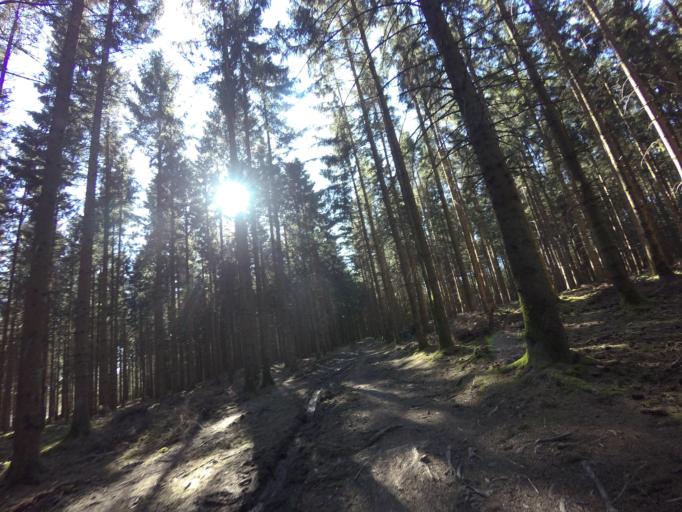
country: BE
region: Wallonia
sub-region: Province de Liege
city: Trois-Ponts
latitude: 50.4040
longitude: 5.8831
